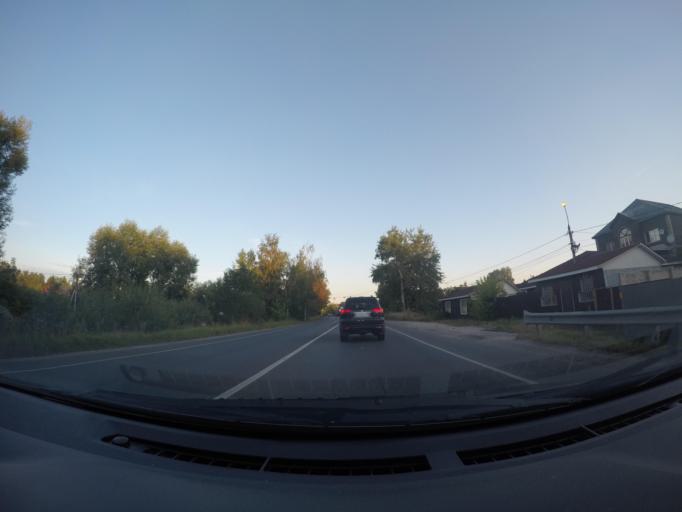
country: RU
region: Moskovskaya
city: Il'inskiy
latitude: 55.6443
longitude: 38.1496
